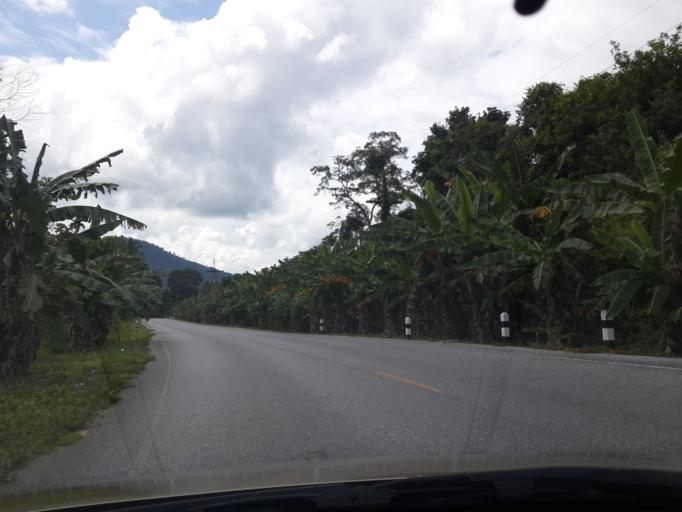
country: TH
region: Yala
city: Raman
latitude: 6.3823
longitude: 101.4018
